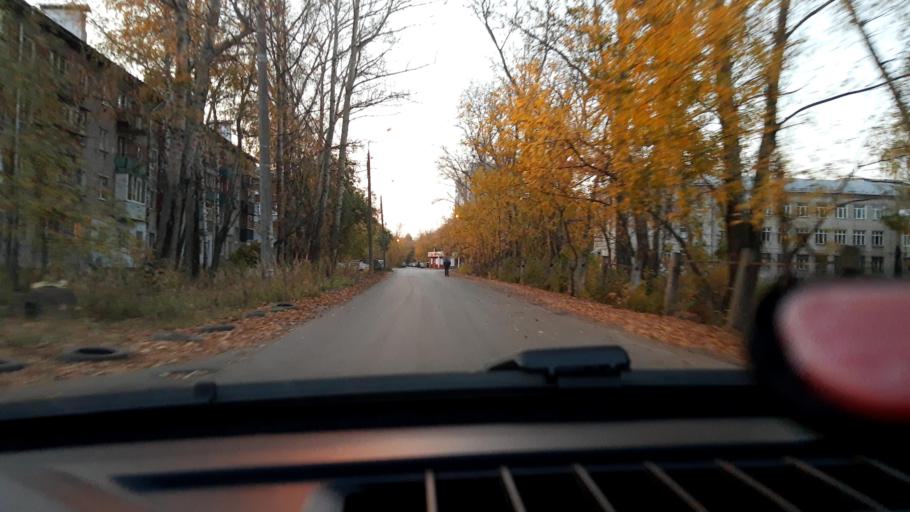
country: RU
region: Nizjnij Novgorod
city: Nizhniy Novgorod
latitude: 56.3039
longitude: 43.8806
